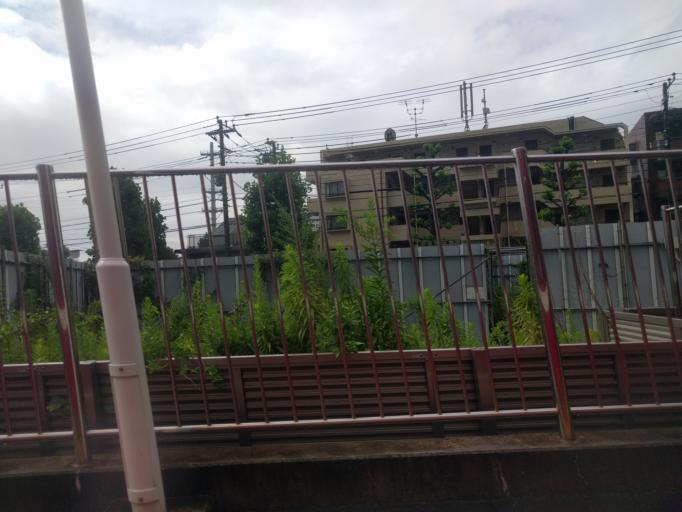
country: JP
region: Kanagawa
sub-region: Kawasaki-shi
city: Kawasaki
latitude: 35.5349
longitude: 139.7129
